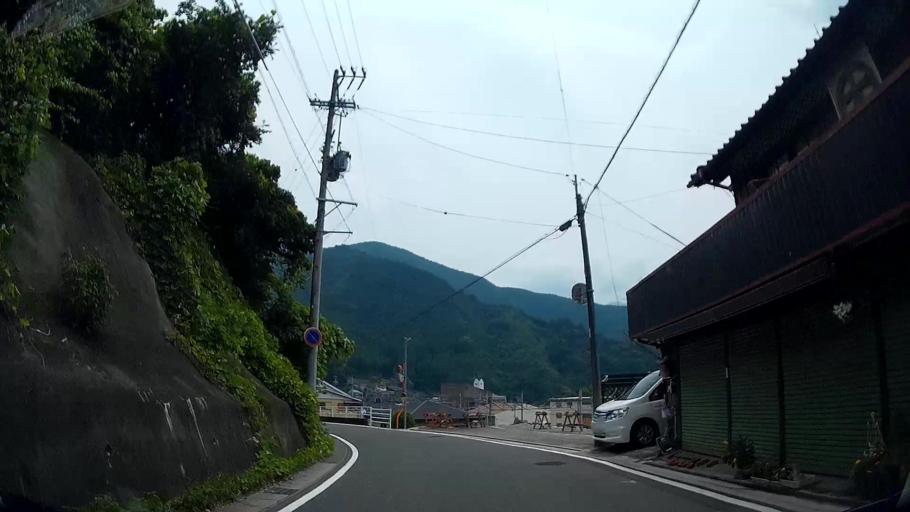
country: JP
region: Shizuoka
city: Mori
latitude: 35.0925
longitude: 137.8082
